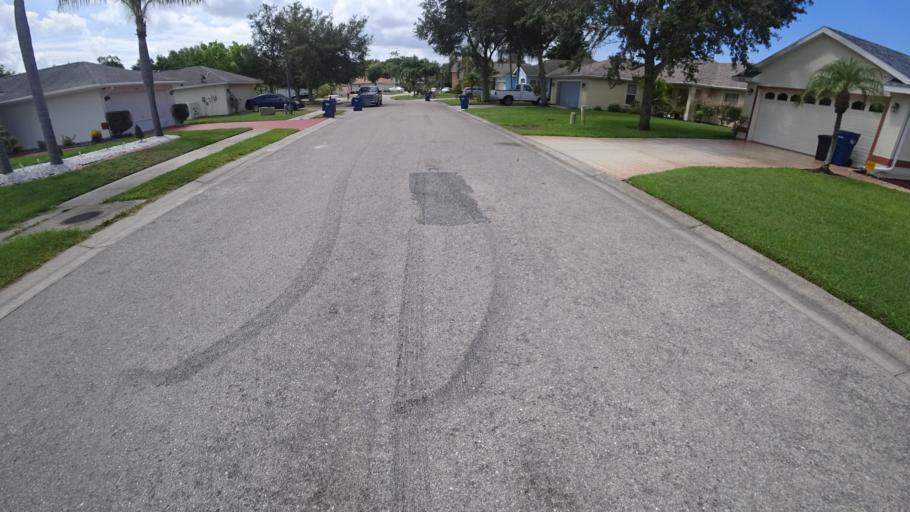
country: US
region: Florida
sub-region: Manatee County
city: Samoset
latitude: 27.4534
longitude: -82.5339
